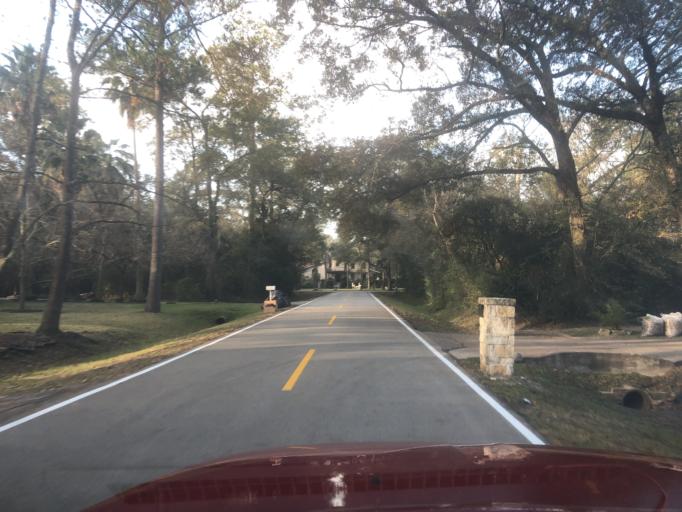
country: US
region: Texas
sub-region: Harris County
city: Spring
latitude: 30.0195
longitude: -95.4772
